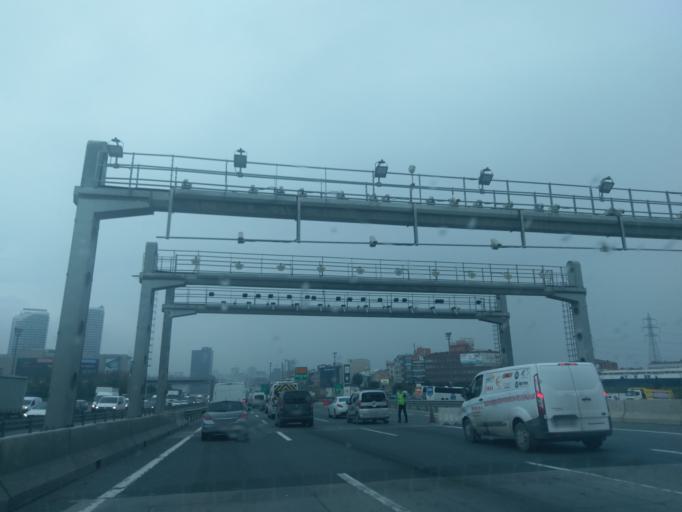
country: TR
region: Istanbul
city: Mahmutbey
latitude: 41.0630
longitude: 28.7993
